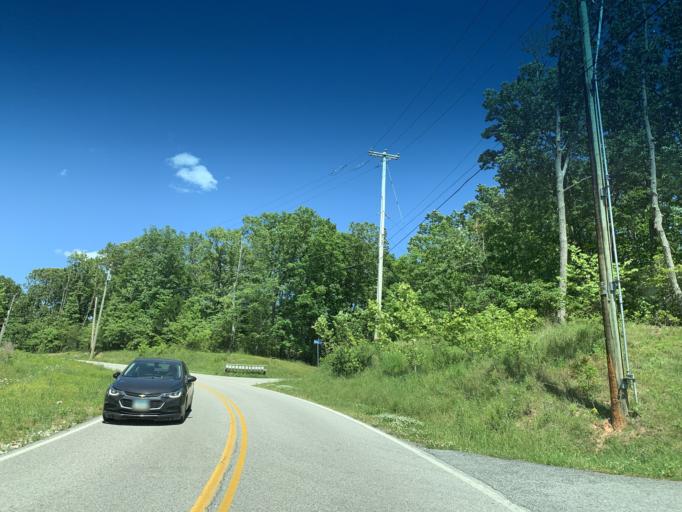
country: US
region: Maryland
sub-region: Cecil County
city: Charlestown
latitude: 39.5215
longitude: -75.9404
